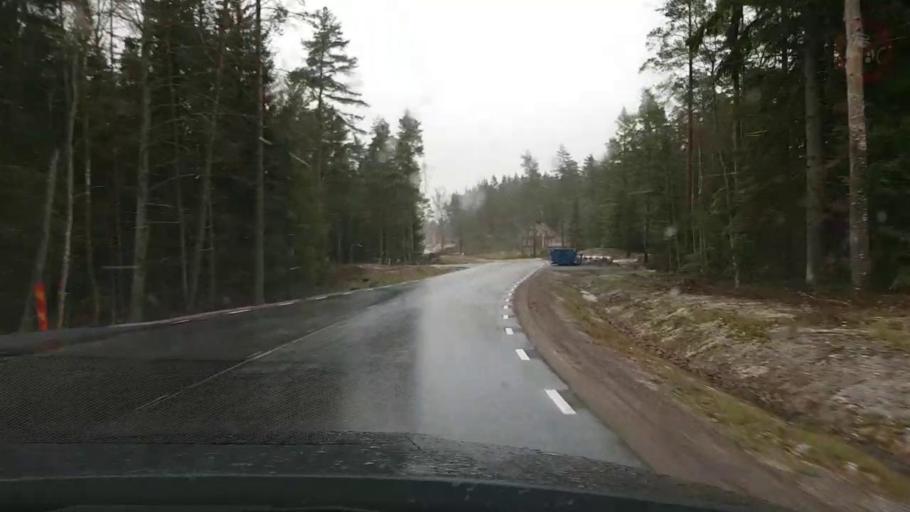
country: SE
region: Vaestra Goetaland
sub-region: Karlsborgs Kommun
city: Karlsborg
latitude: 58.7043
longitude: 14.4999
